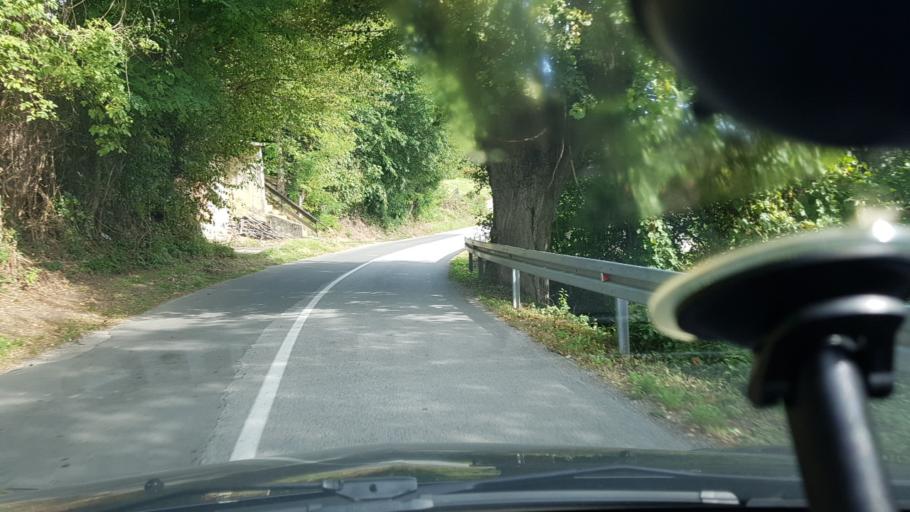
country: HR
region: Varazdinska
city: Remetinec
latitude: 46.1094
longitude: 16.2217
